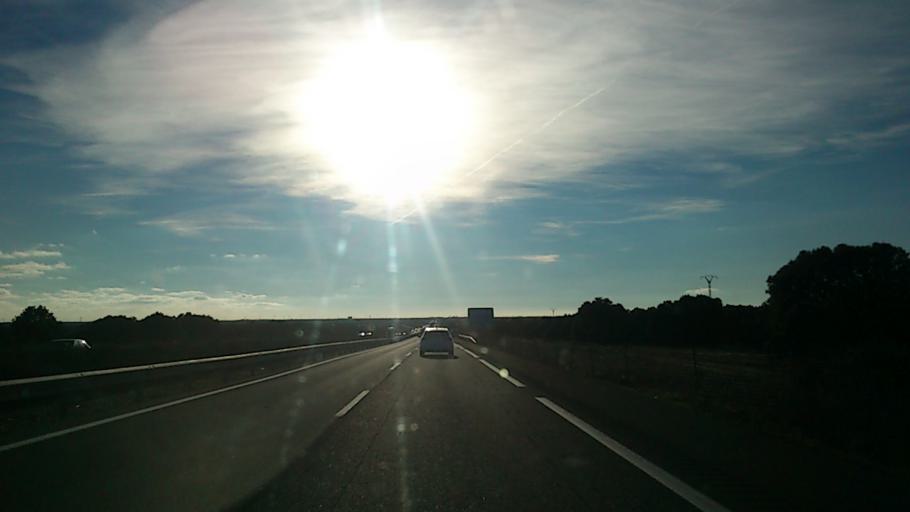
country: ES
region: Castille-La Mancha
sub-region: Provincia de Guadalajara
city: Mirabueno
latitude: 40.9395
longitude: -2.7013
